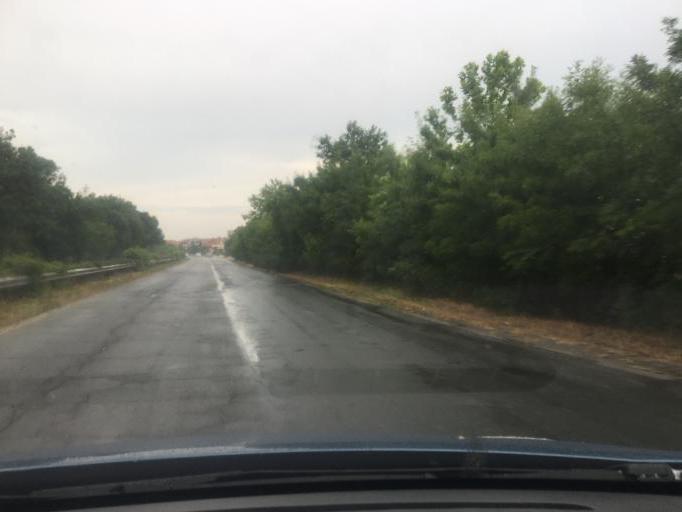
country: BG
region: Burgas
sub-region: Obshtina Burgas
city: Burgas
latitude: 42.5566
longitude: 27.5131
